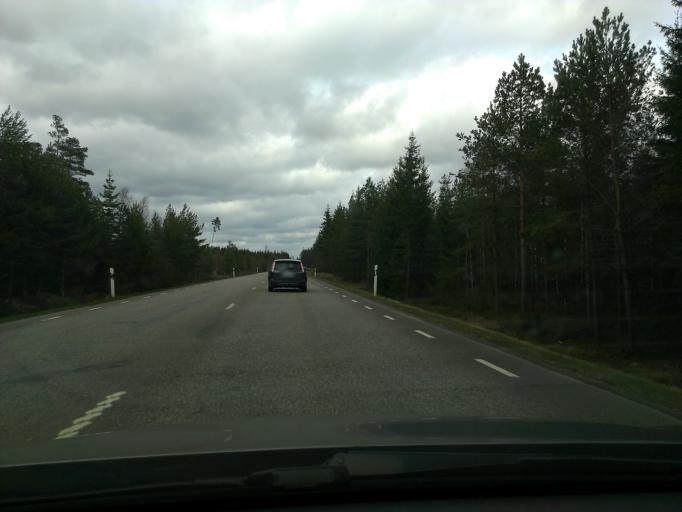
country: SE
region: Kronoberg
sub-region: Almhults Kommun
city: AElmhult
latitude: 56.6212
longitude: 14.2426
